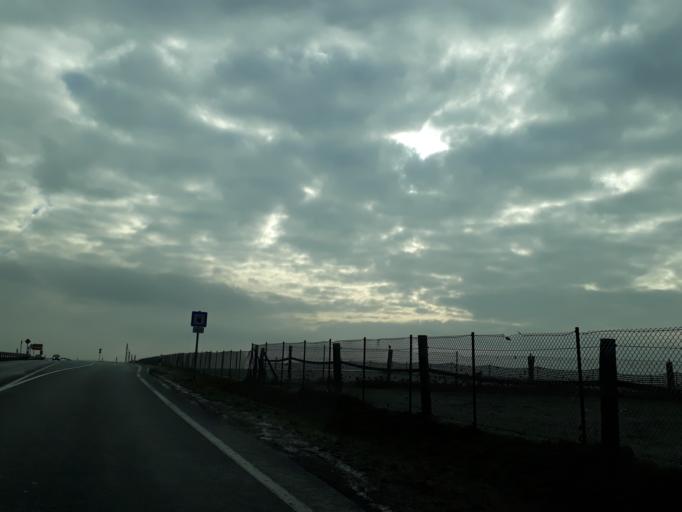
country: DE
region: Saxony
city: Lobau
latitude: 51.1136
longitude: 14.6463
